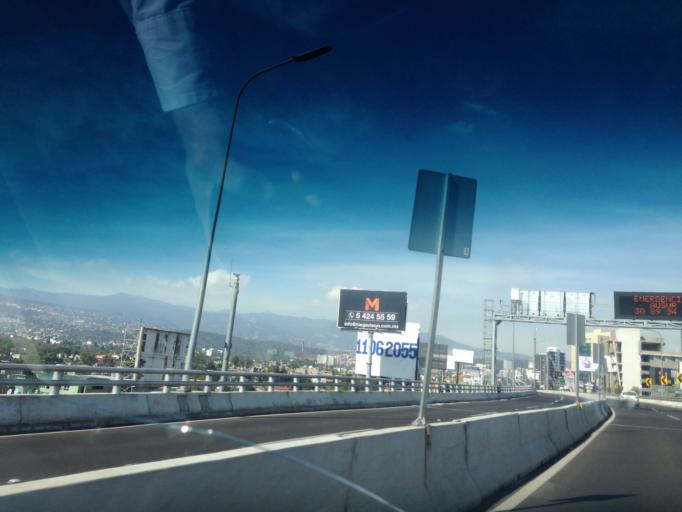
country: MX
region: Mexico City
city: Tlalpan
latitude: 19.3009
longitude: -99.1610
